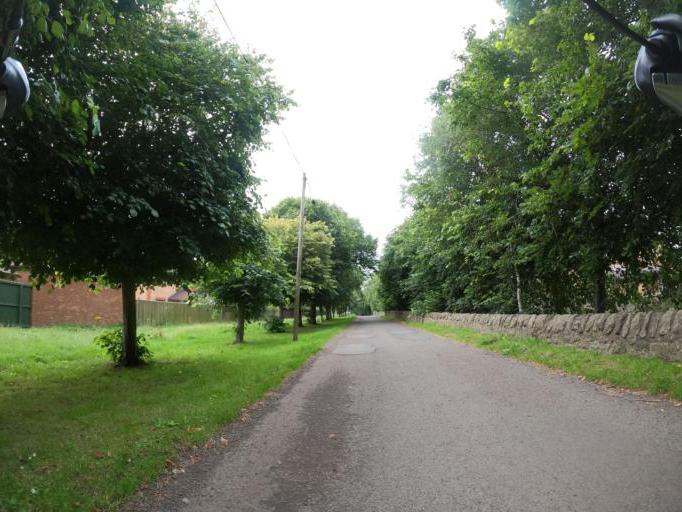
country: GB
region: Scotland
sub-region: East Lothian
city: Musselburgh
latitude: 55.9406
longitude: -3.0957
